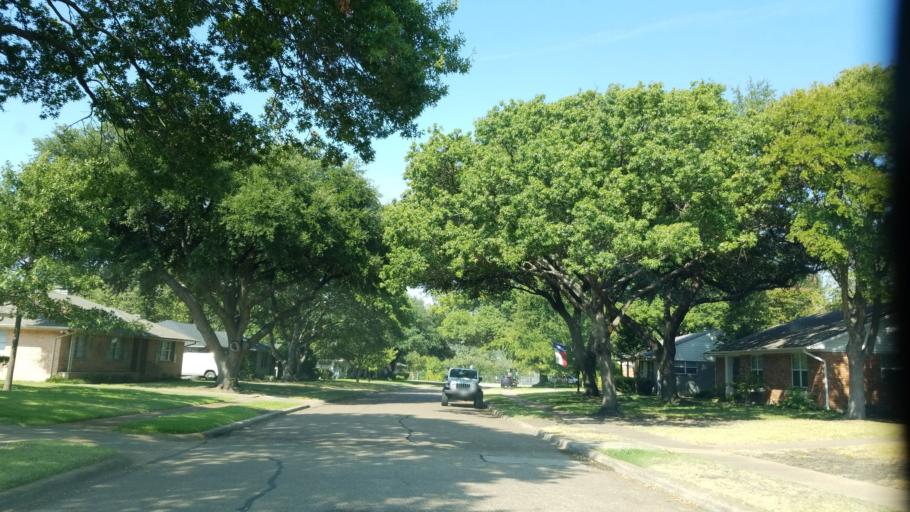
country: US
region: Texas
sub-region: Dallas County
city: Richardson
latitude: 32.9591
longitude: -96.7420
